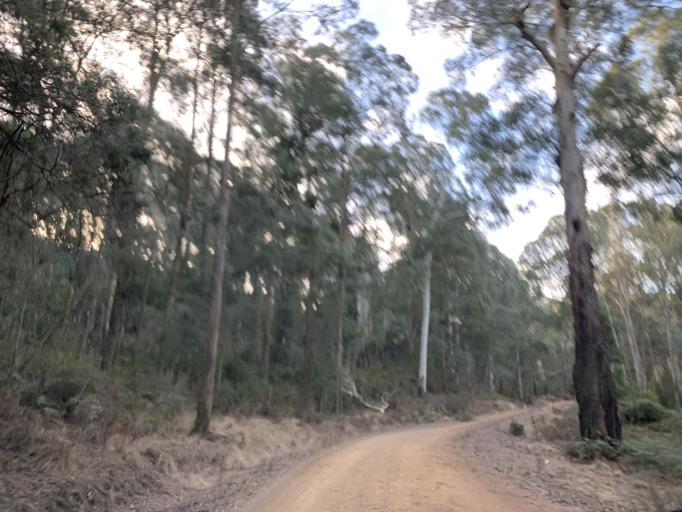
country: AU
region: Victoria
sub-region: Mansfield
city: Mansfield
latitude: -36.8871
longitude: 146.1207
